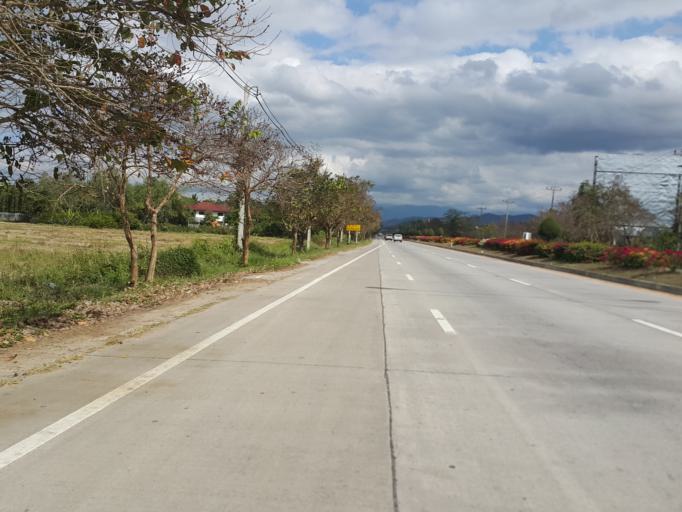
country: TH
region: Chiang Mai
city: San Sai
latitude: 18.8596
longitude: 99.1073
